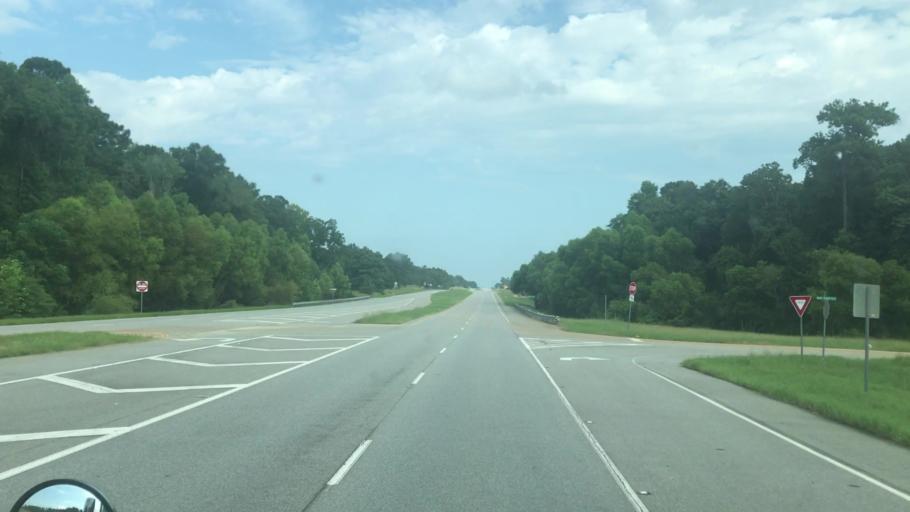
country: US
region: Georgia
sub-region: Early County
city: Blakely
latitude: 31.3000
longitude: -84.8592
